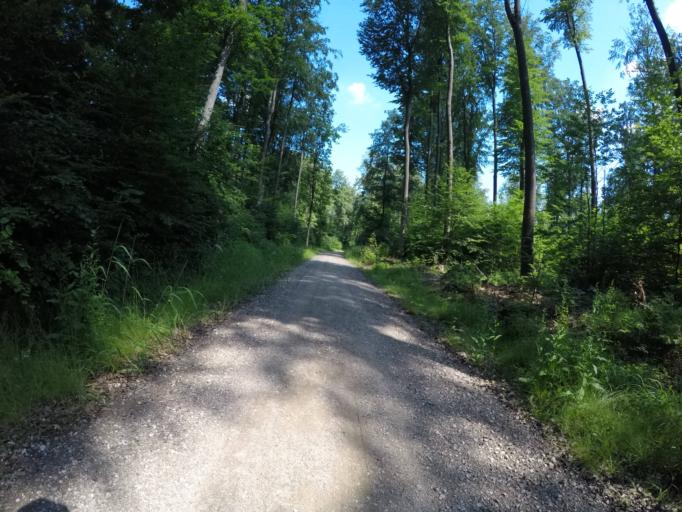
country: DE
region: Bavaria
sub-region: Lower Bavaria
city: Essing
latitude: 48.9092
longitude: 11.8273
